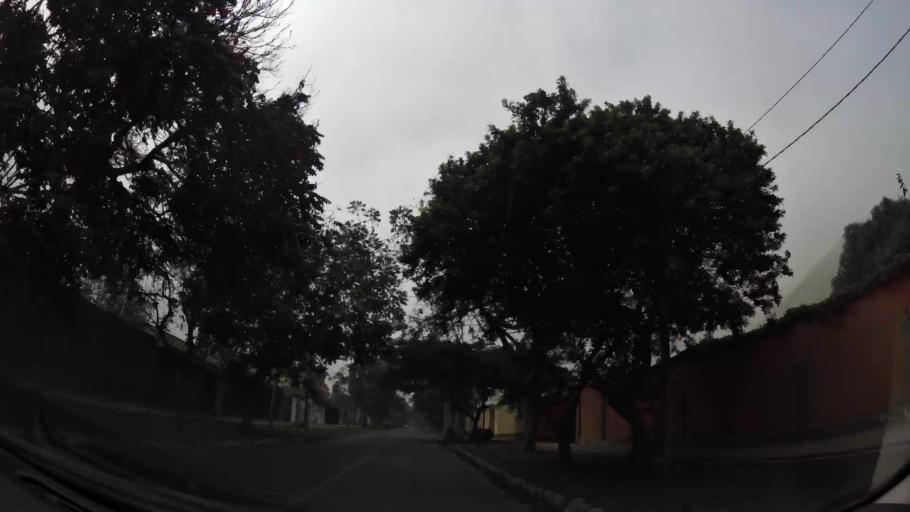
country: PE
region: Lima
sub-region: Lima
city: Chaclacayo
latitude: -11.9790
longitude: -76.7712
